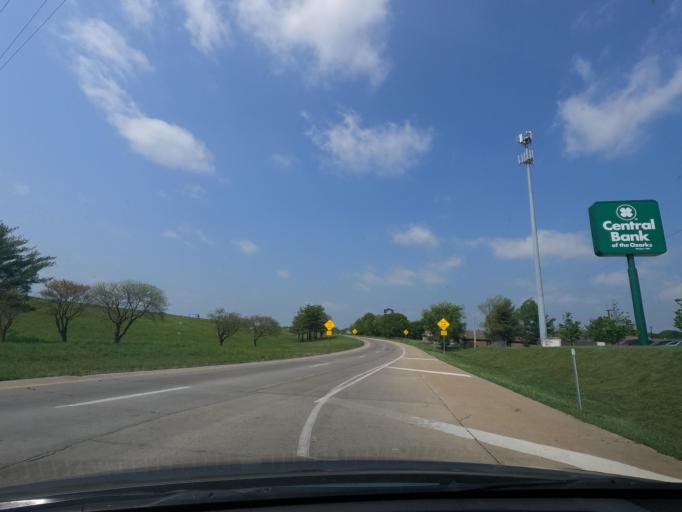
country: US
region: Missouri
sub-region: Greene County
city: Battlefield
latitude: 37.1373
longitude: -93.2967
